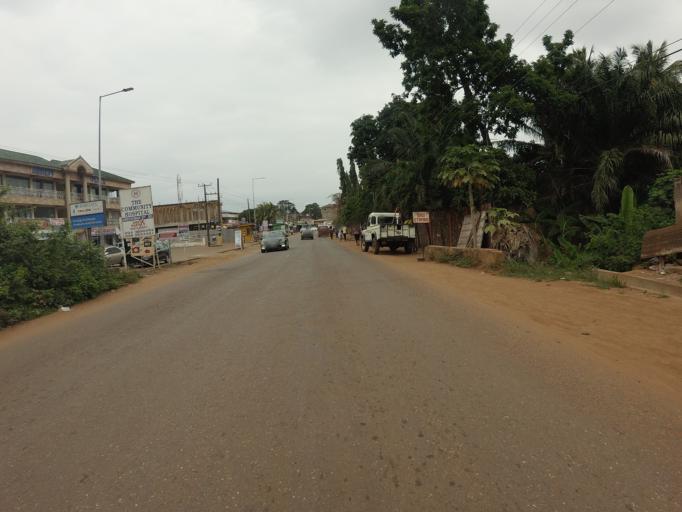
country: GH
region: Greater Accra
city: Dome
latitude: 5.6657
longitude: -0.2047
